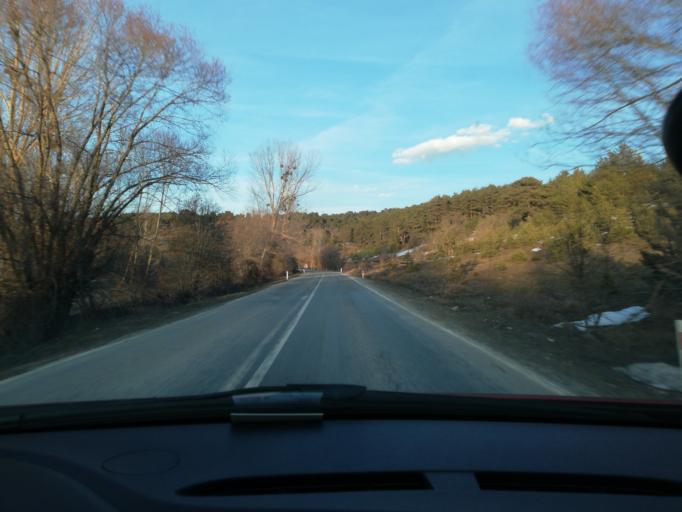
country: TR
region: Kastamonu
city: Agli
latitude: 41.7048
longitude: 33.6491
